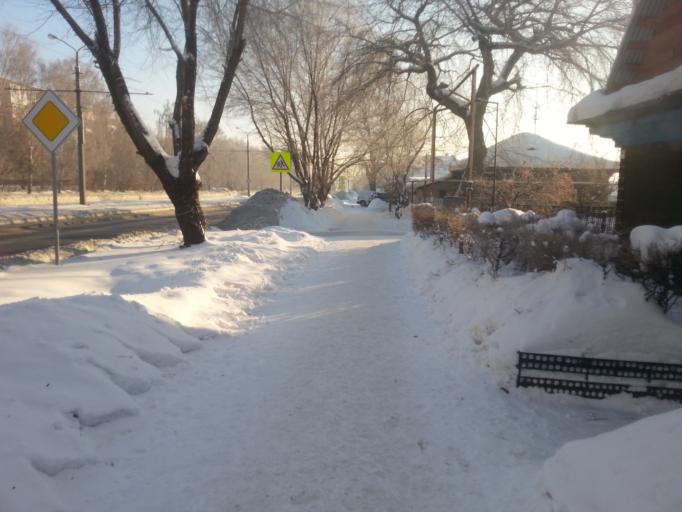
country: RU
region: Altai Krai
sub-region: Gorod Barnaulskiy
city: Barnaul
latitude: 53.3533
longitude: 83.7226
